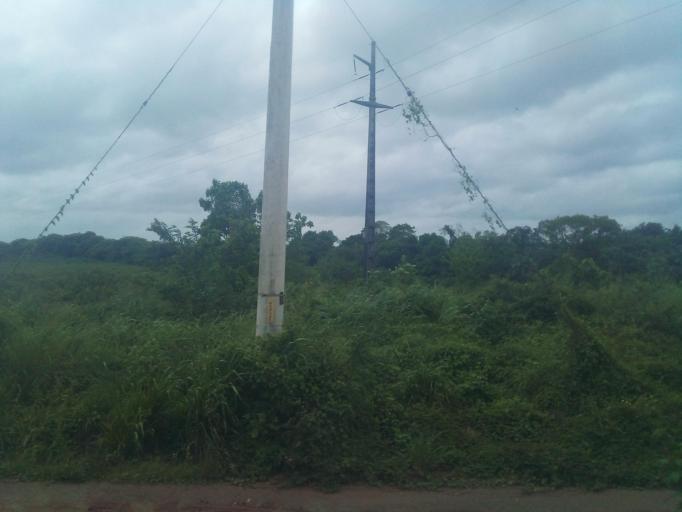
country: BR
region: Maranhao
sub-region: Arari
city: Arari
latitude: -3.5712
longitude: -44.6880
